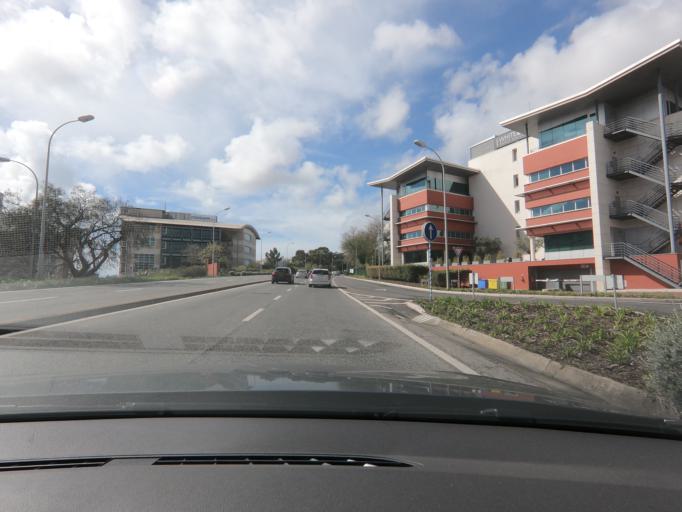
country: PT
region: Lisbon
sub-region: Oeiras
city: Porto Salvo
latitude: 38.7118
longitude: -9.2980
